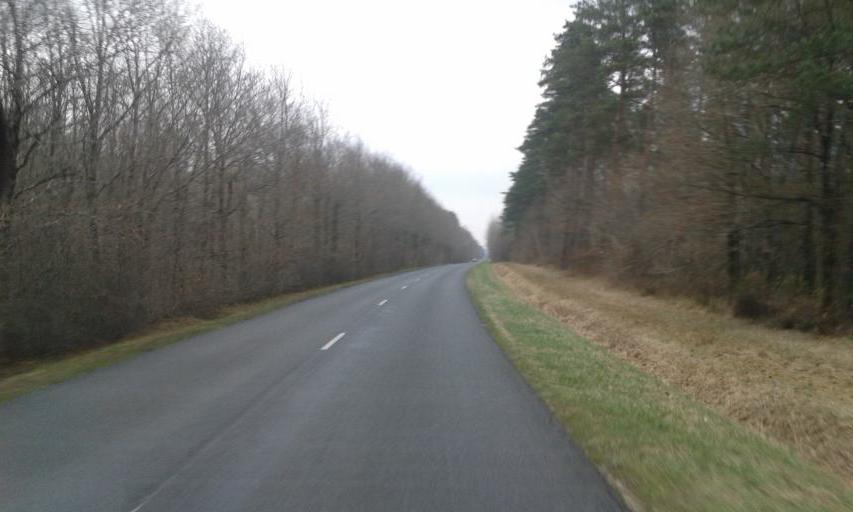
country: FR
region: Centre
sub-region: Departement du Loir-et-Cher
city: Dhuizon
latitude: 47.6204
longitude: 1.6615
